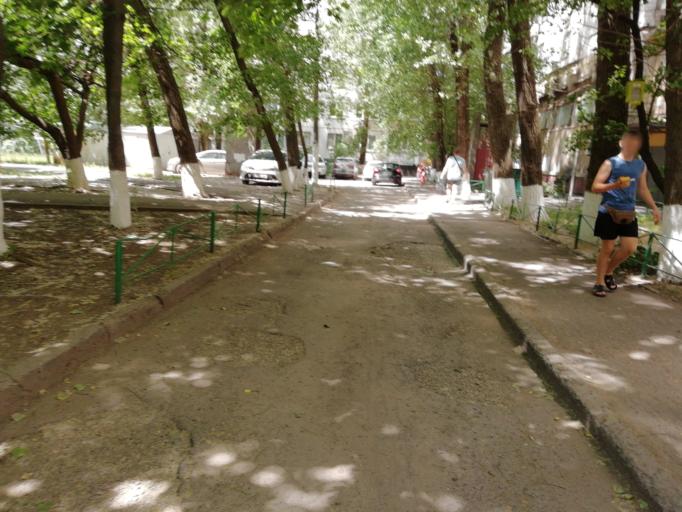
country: RU
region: Rostov
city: Severnyy
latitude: 47.2873
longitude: 39.7096
